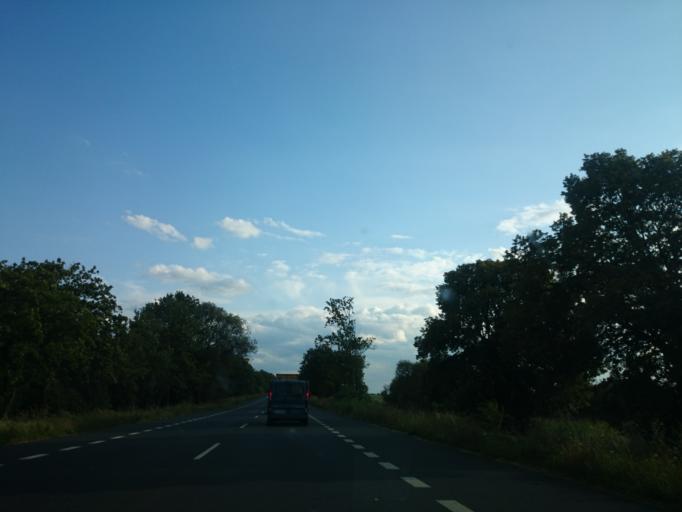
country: PL
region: West Pomeranian Voivodeship
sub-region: Powiat pyrzycki
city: Lipiany
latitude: 52.9840
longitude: 14.9783
